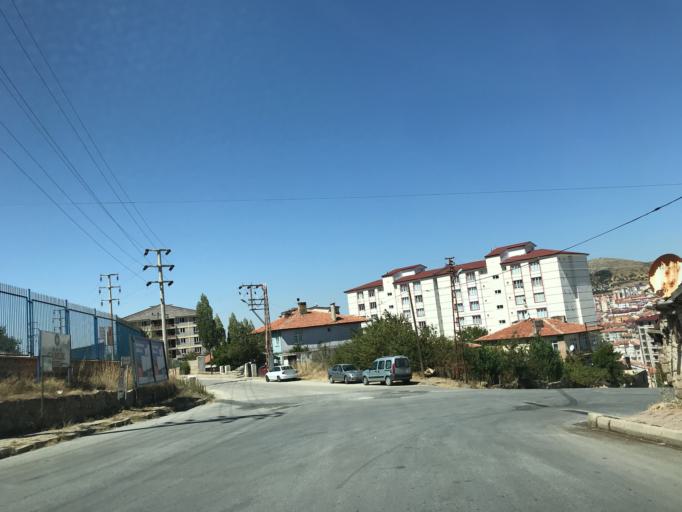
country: TR
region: Yozgat
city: Yozgat
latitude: 39.8185
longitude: 34.8175
